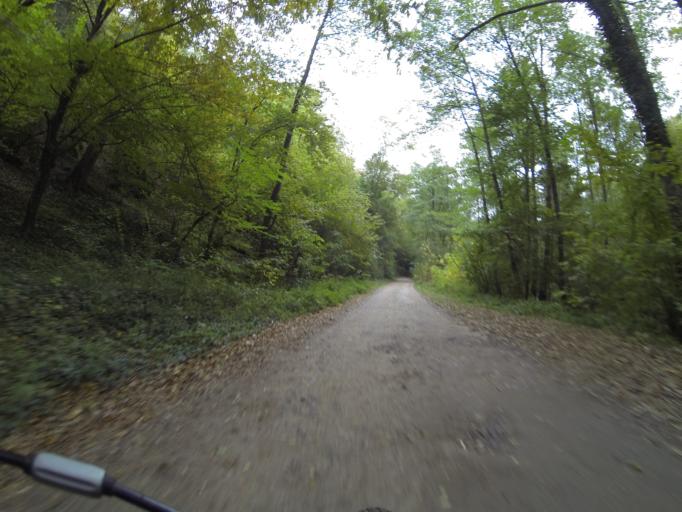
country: RO
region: Gorj
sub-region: Comuna Tismana
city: Pocruia
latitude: 45.0533
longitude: 22.9139
